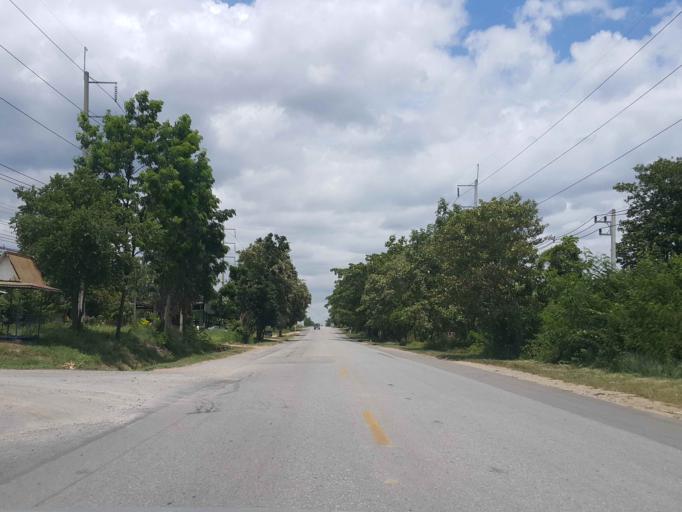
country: TH
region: Lamphun
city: Ban Hong
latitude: 18.3633
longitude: 98.8116
